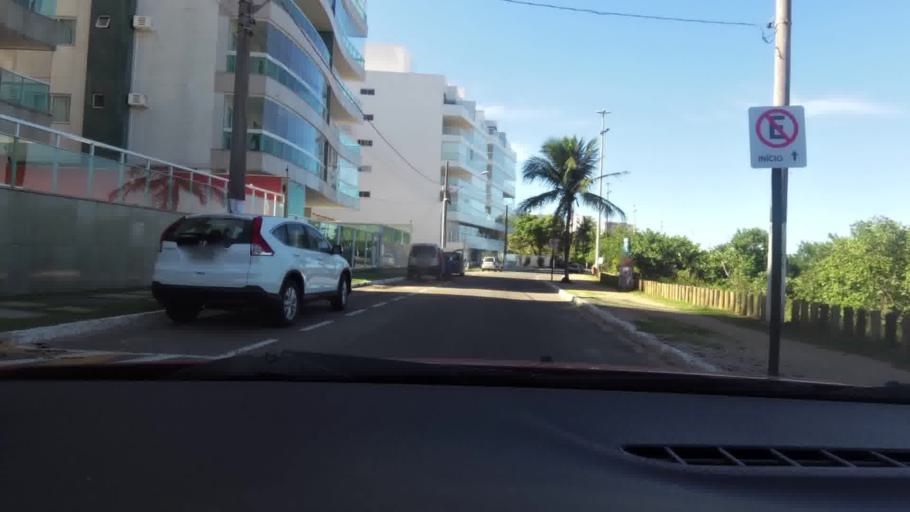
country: BR
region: Espirito Santo
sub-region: Guarapari
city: Guarapari
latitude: -20.7334
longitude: -40.5316
